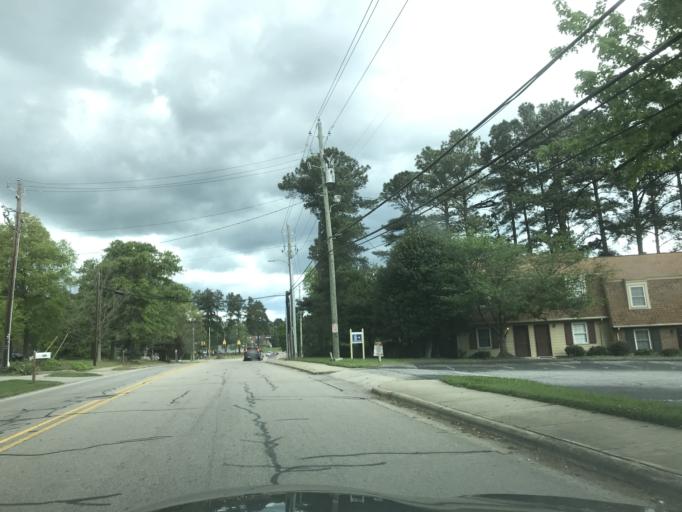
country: US
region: North Carolina
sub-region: Wake County
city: West Raleigh
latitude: 35.7822
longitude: -78.7214
